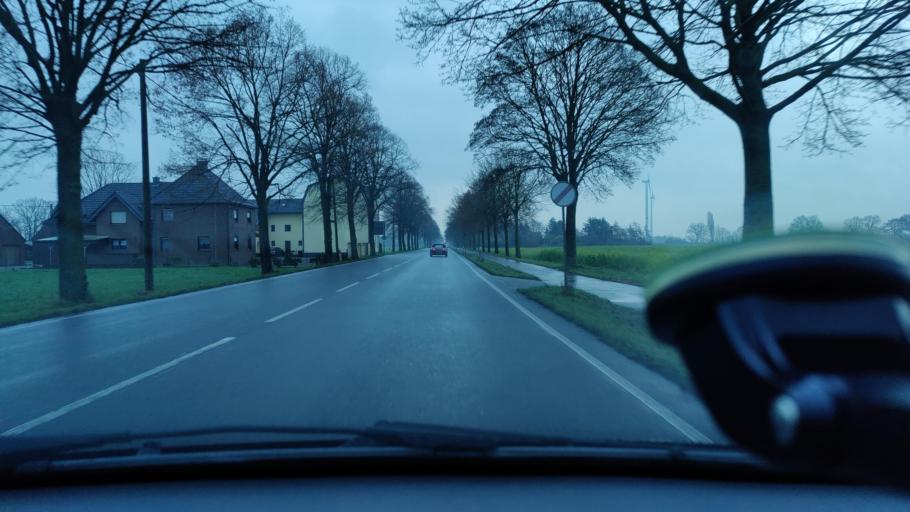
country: DE
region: North Rhine-Westphalia
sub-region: Regierungsbezirk Dusseldorf
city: Alpen
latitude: 51.5880
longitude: 6.5446
